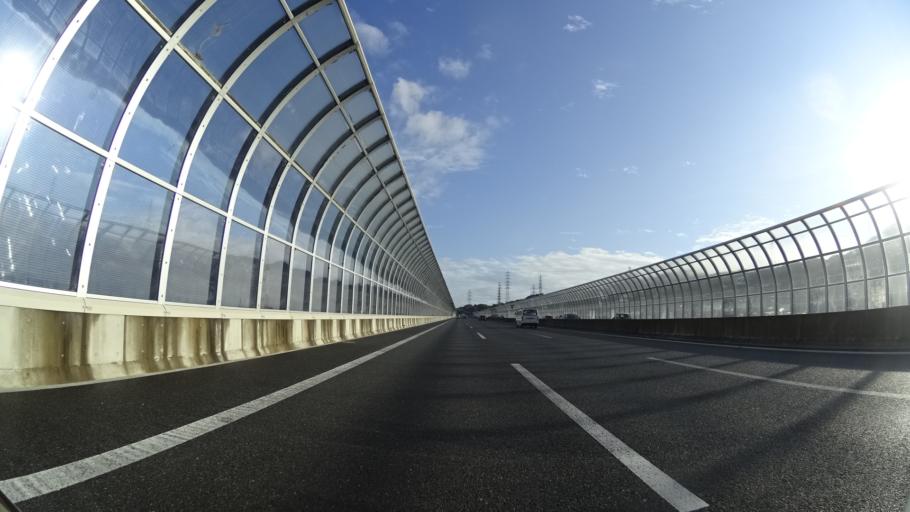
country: JP
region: Osaka
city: Hirakata
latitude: 34.7909
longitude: 135.6941
